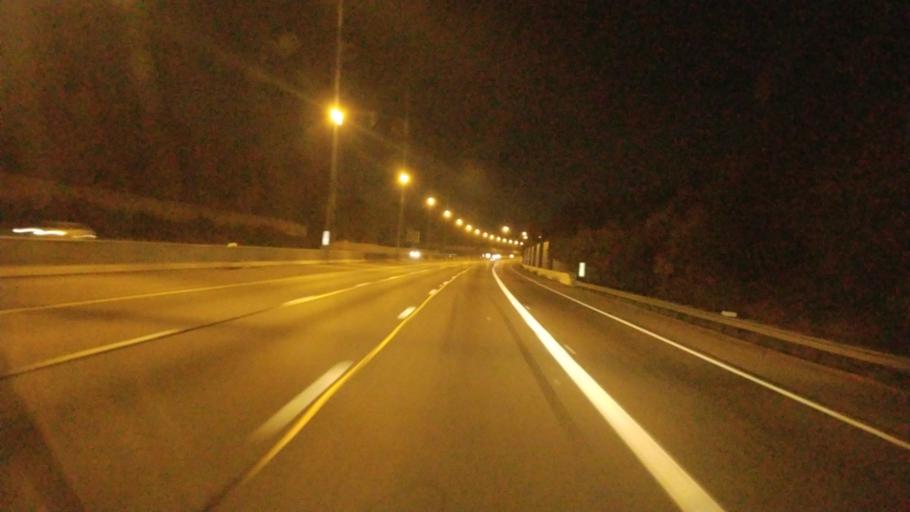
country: US
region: Ohio
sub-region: Franklin County
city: Westerville
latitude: 40.1238
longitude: -82.9729
